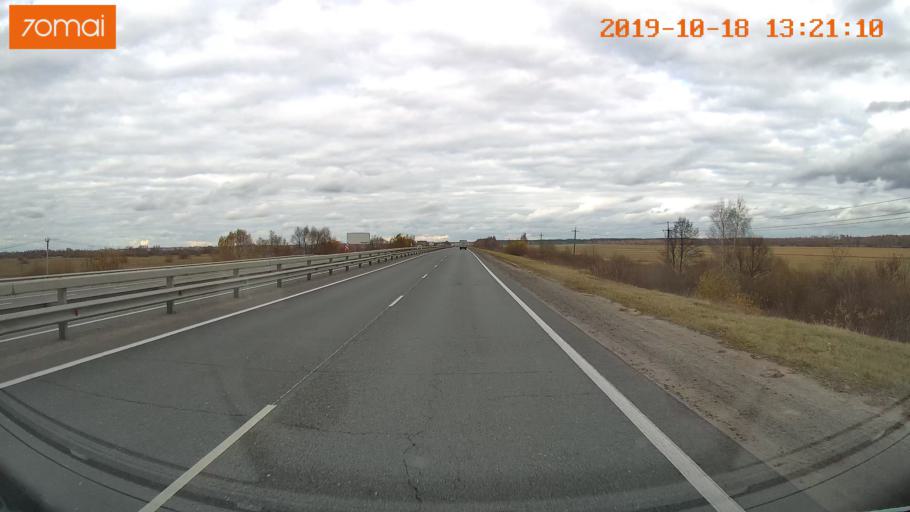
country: RU
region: Rjazan
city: Polyany
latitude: 54.6935
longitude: 39.8386
